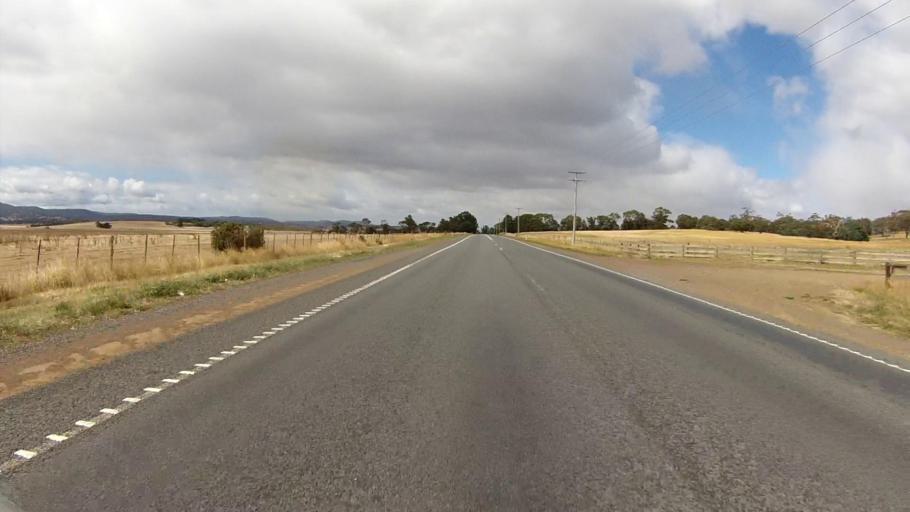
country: AU
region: Tasmania
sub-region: Northern Midlands
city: Evandale
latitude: -41.9785
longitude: 147.5045
